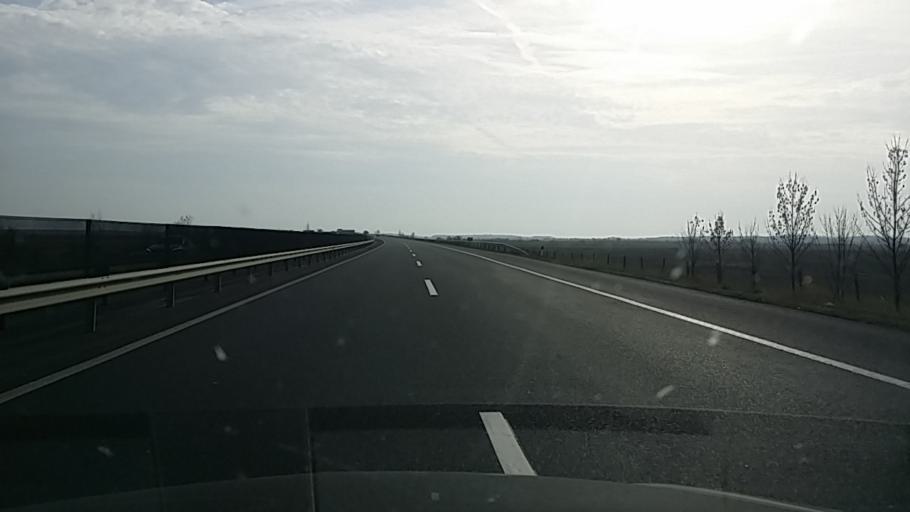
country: HU
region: Hajdu-Bihar
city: Polgar
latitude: 47.8313
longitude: 21.1511
